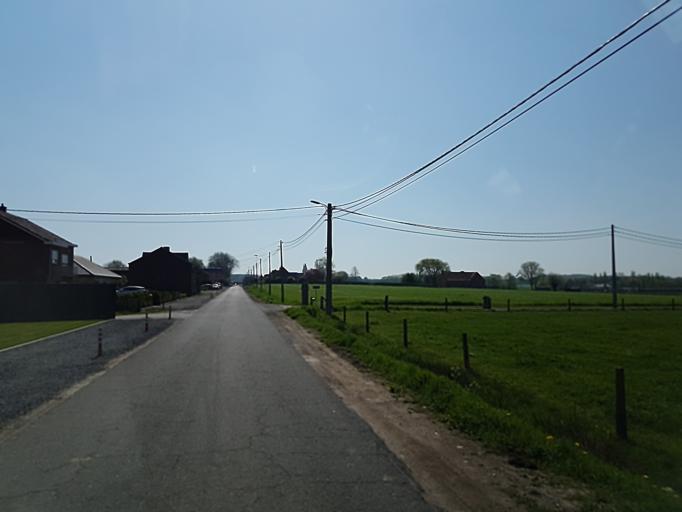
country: BE
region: Flanders
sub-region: Provincie West-Vlaanderen
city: Zonnebeke
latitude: 50.8612
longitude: 2.9559
